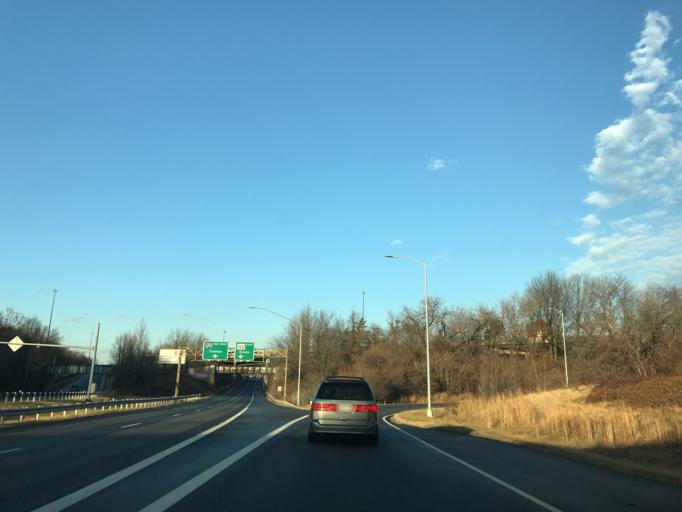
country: US
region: Maryland
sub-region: Baltimore County
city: Rosedale
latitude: 39.2901
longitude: -76.5041
